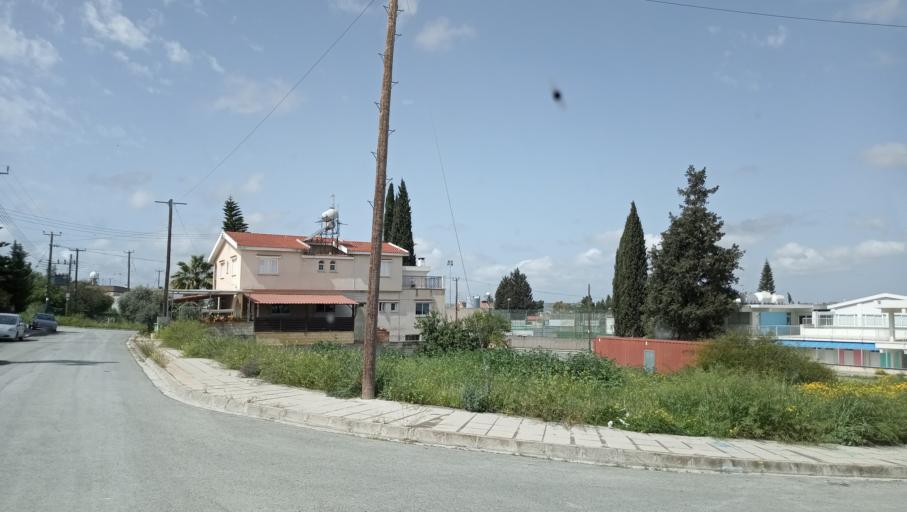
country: CY
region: Lefkosia
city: Dali
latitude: 35.0157
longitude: 33.4212
